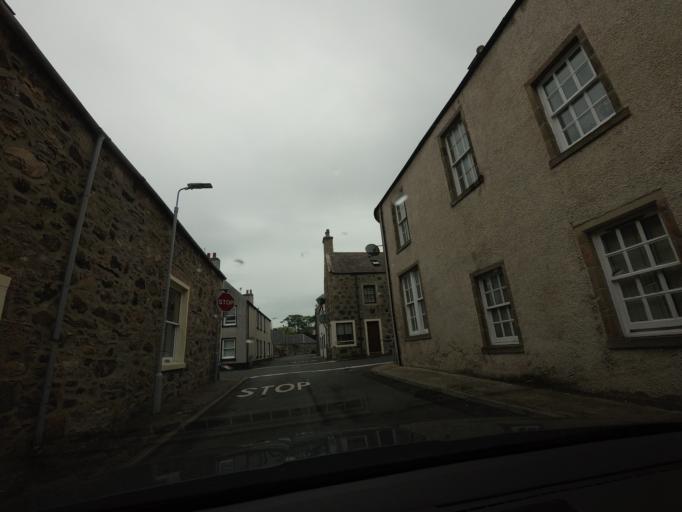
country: GB
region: Scotland
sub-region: Aberdeenshire
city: Portsoy
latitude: 57.6836
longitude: -2.6902
